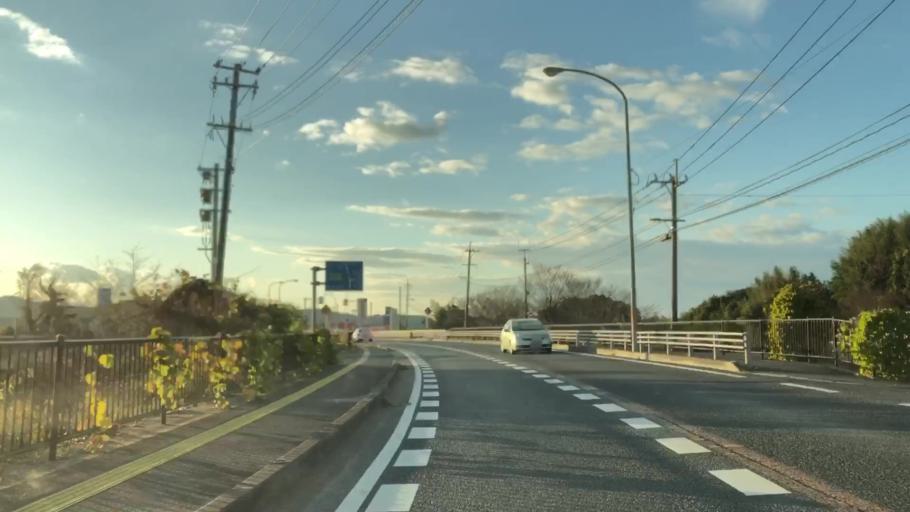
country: JP
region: Fukuoka
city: Nakatsu
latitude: 33.5389
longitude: 131.2979
